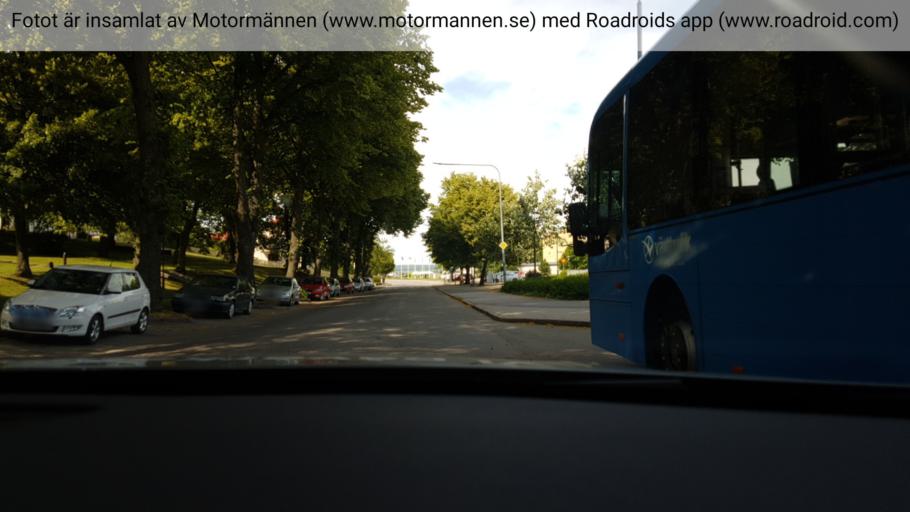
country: SE
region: Vaestra Goetaland
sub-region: Mariestads Kommun
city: Mariestad
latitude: 58.7117
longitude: 13.8240
